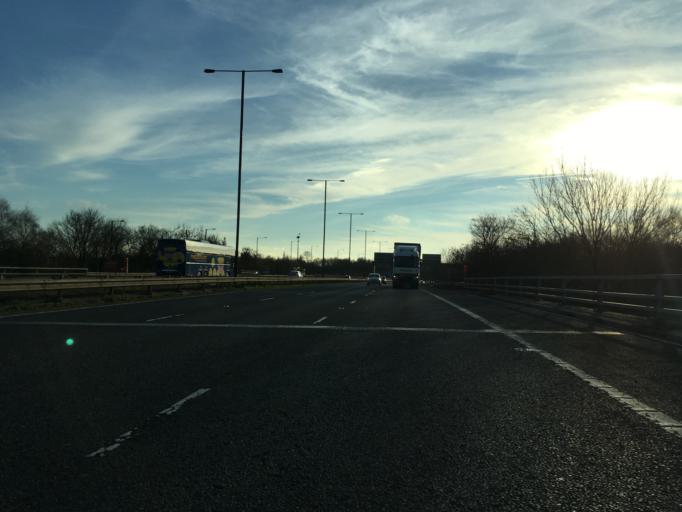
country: GB
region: England
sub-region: Manchester
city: Chorlton cum Hardy
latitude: 53.3988
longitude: -2.2690
